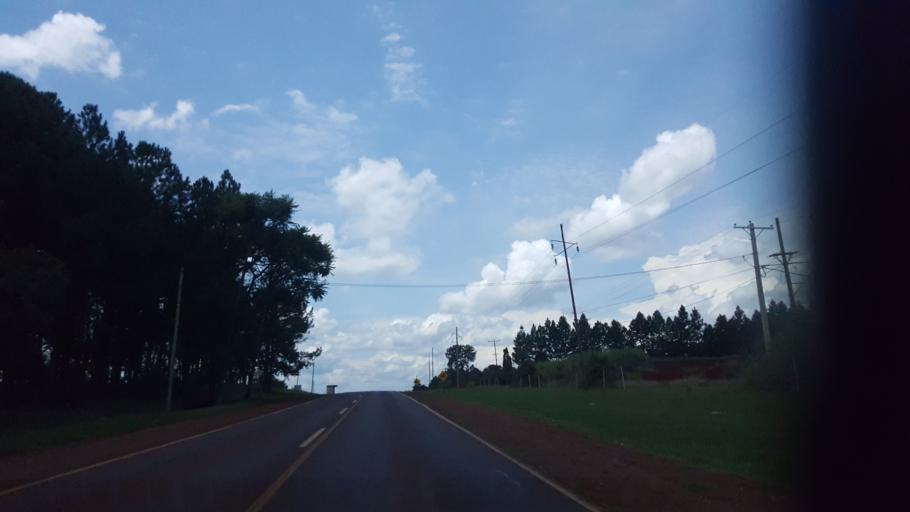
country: AR
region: Misiones
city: Puerto Rico
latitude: -26.8208
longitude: -55.0127
